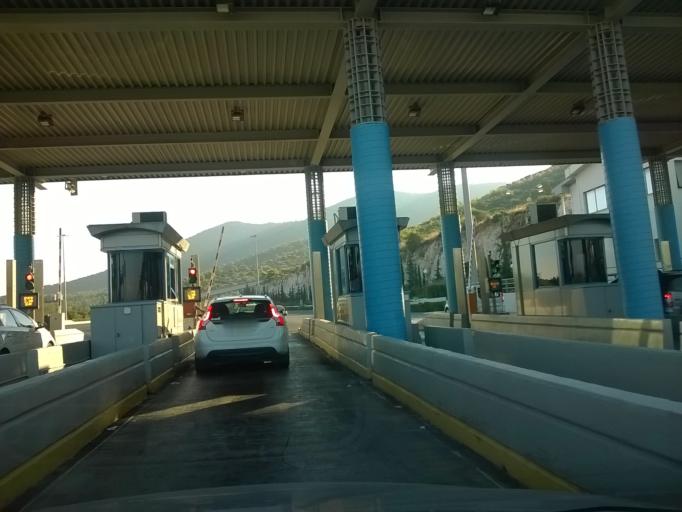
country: GR
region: Attica
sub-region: Nomos Attikis
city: Zografos
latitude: 37.9770
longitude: 23.8001
